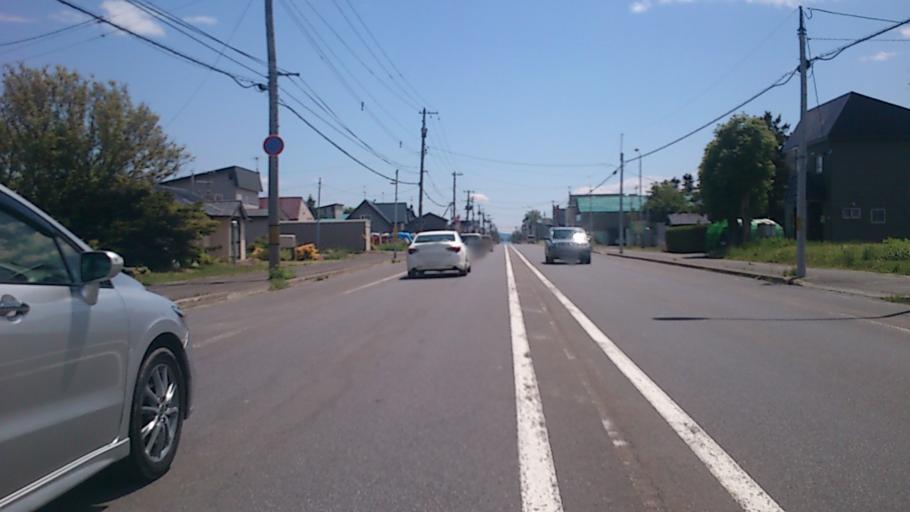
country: JP
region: Hokkaido
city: Nayoro
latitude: 44.2445
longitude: 142.3950
